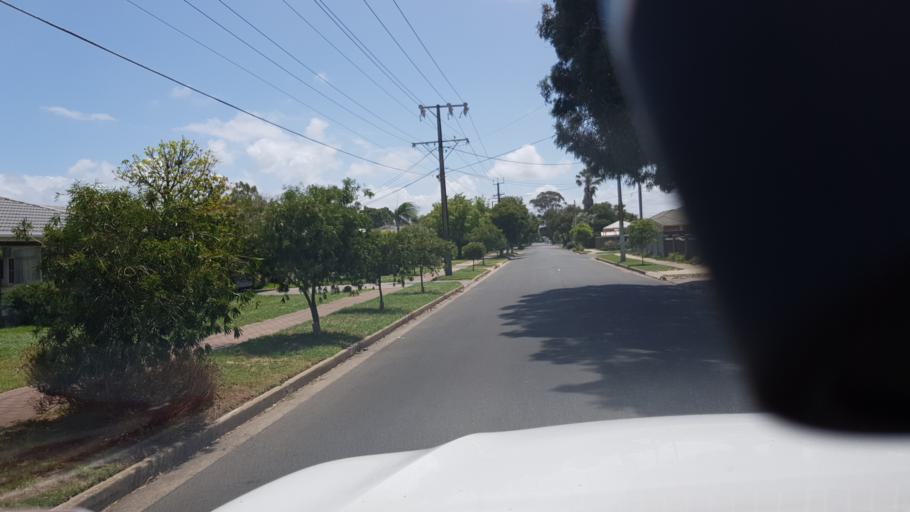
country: AU
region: South Australia
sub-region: Holdfast Bay
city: North Brighton
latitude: -35.0052
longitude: 138.5311
